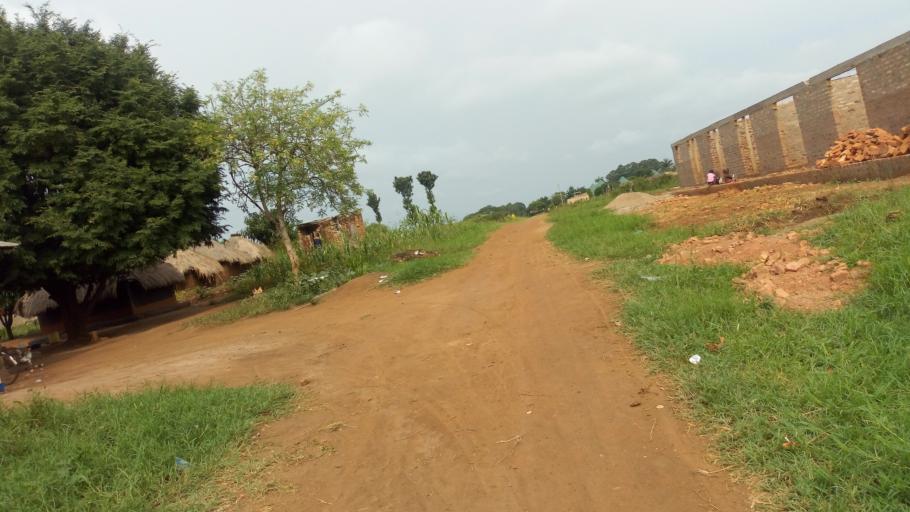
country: UG
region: Western Region
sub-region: Kiryandongo District
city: Kiryandongo
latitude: 1.8016
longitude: 32.0144
